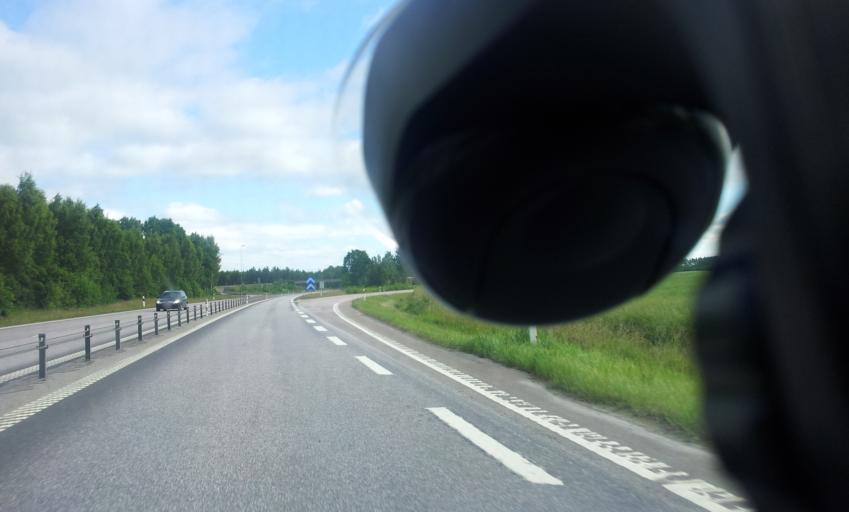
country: SE
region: Kalmar
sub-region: Kalmar Kommun
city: Lindsdal
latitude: 56.7543
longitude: 16.3064
